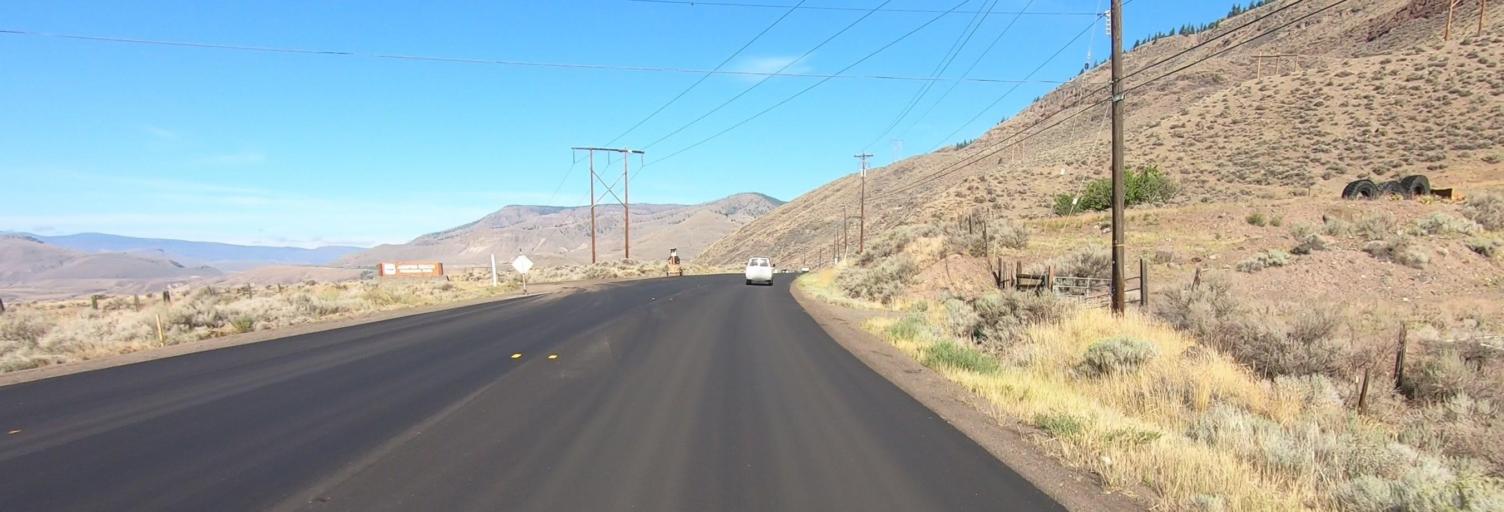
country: CA
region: British Columbia
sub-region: Thompson-Nicola Regional District
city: Ashcroft
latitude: 50.7880
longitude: -121.0723
